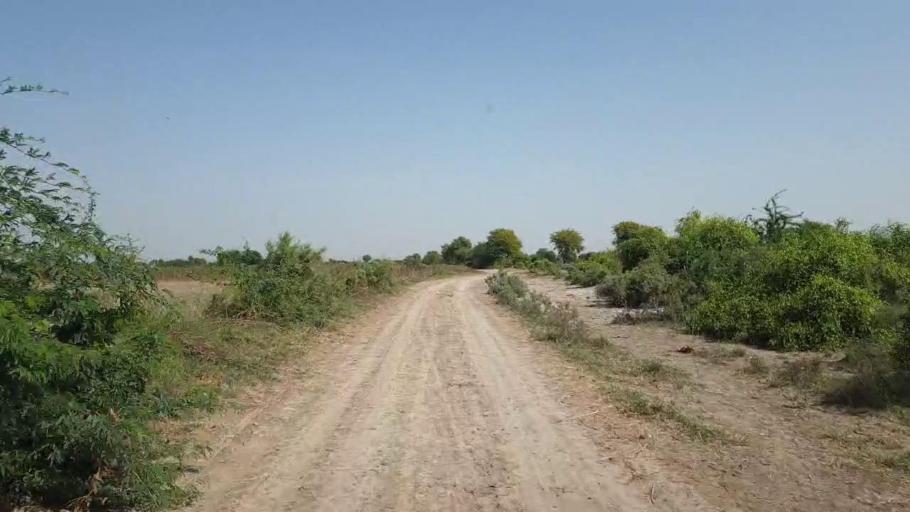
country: PK
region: Sindh
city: Tando Bago
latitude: 24.7214
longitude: 69.0226
